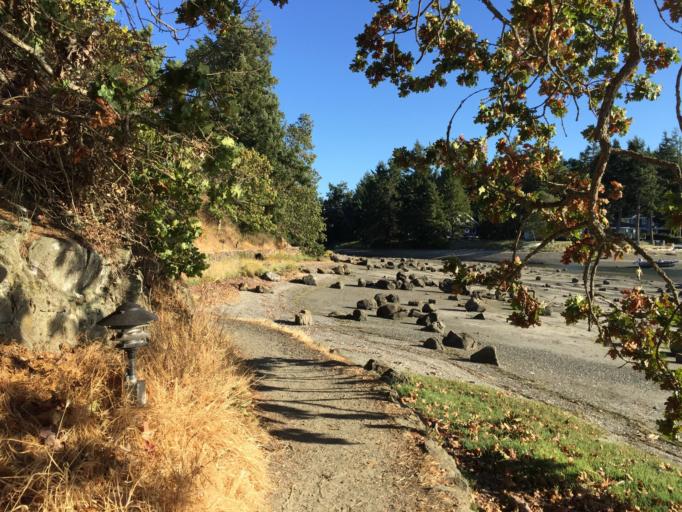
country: CA
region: British Columbia
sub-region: Regional District of Nanaimo
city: Parksville
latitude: 49.3065
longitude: -124.2403
